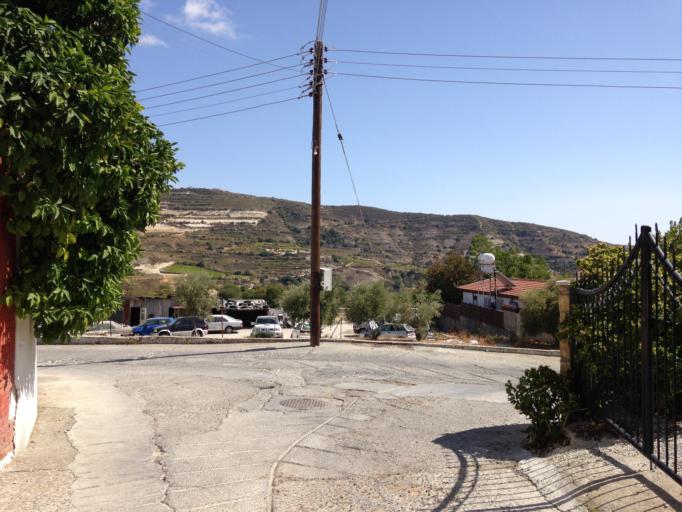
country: CY
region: Limassol
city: Pachna
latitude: 34.8469
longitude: 32.8096
